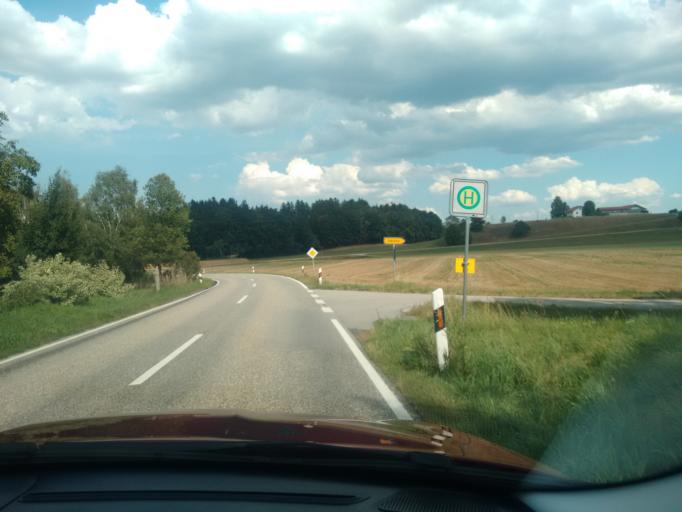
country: DE
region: Bavaria
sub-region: Upper Bavaria
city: Halsbach
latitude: 48.1185
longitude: 12.7140
